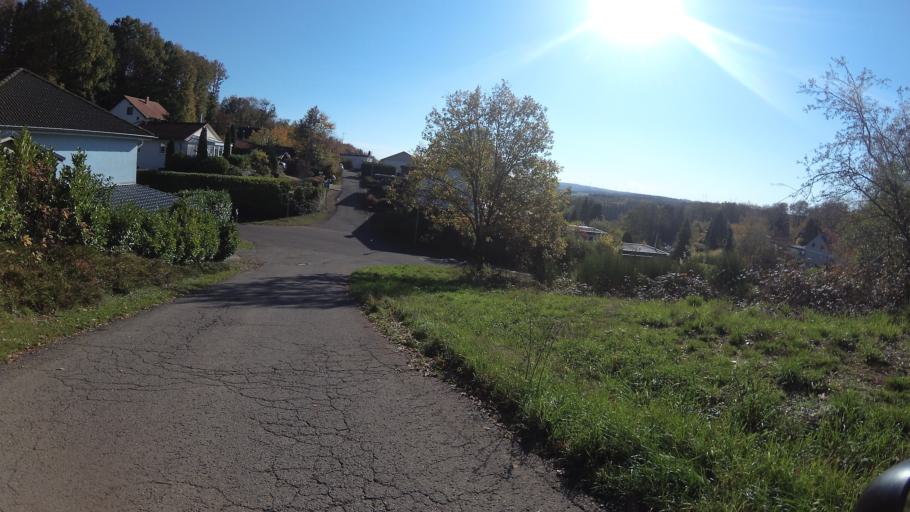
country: DE
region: Saarland
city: Weiskirchen
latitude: 49.5442
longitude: 6.7740
